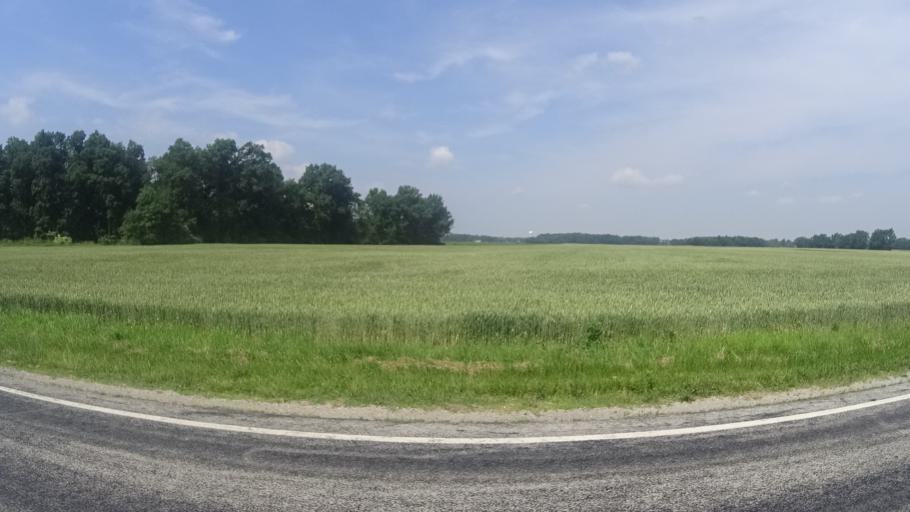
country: US
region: Ohio
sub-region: Huron County
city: Monroeville
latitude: 41.3395
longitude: -82.7229
